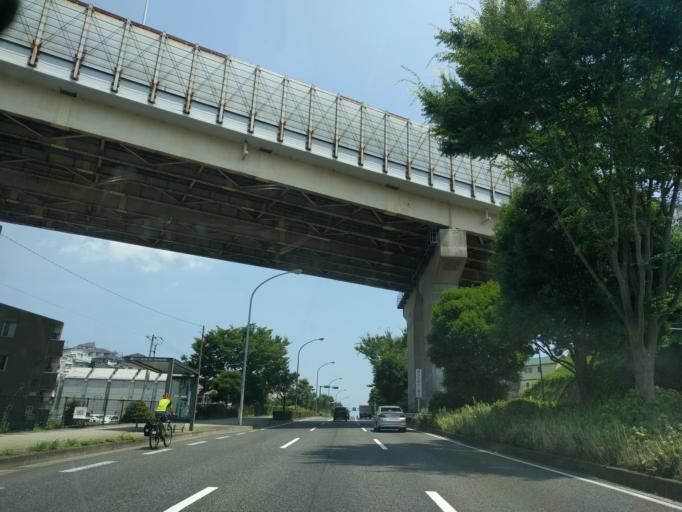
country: JP
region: Kanagawa
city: Yokohama
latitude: 35.4016
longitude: 139.5756
